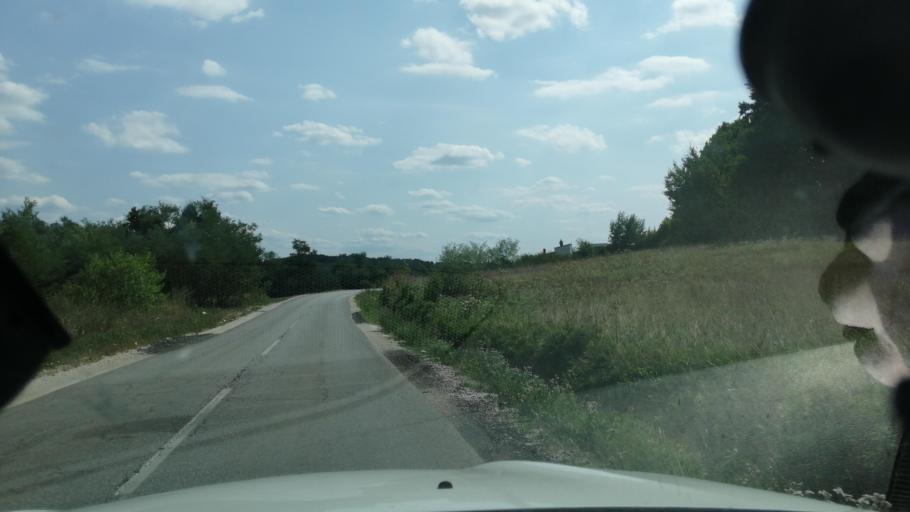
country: RS
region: Central Serbia
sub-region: Moravicki Okrug
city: Lucani
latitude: 43.7979
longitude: 20.2549
